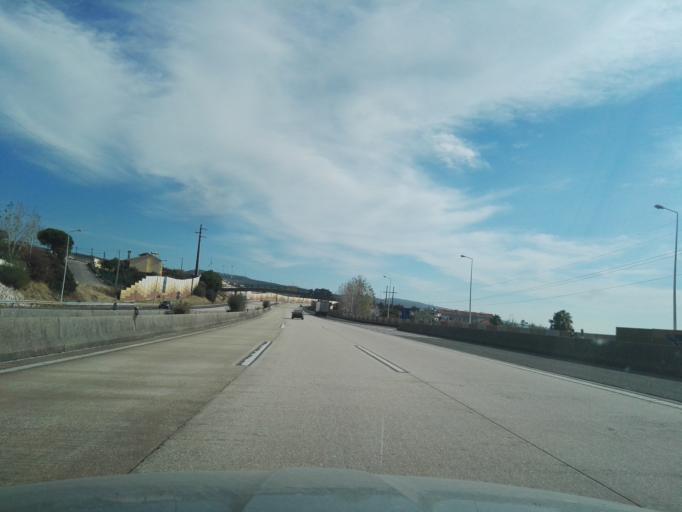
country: PT
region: Lisbon
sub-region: Loures
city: Loures
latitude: 38.8521
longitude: -9.1728
